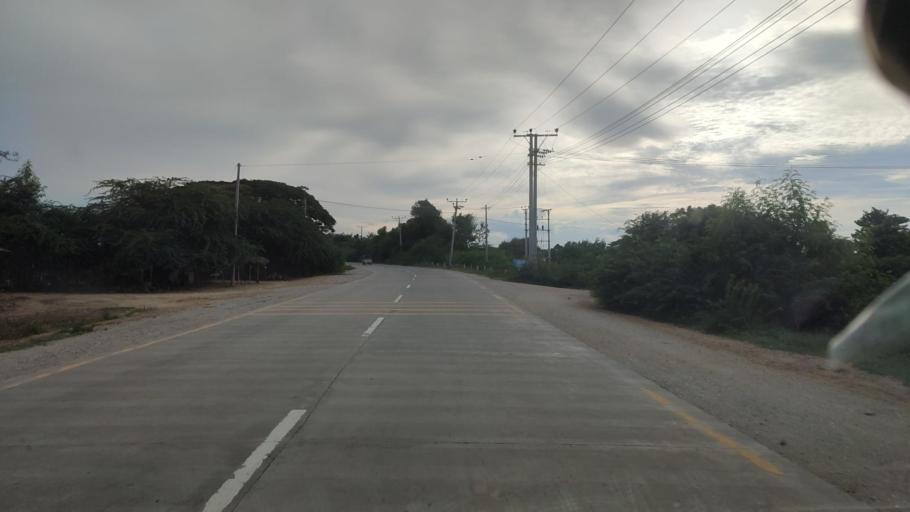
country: MM
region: Mandalay
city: Kyaukse
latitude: 21.3365
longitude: 96.0568
